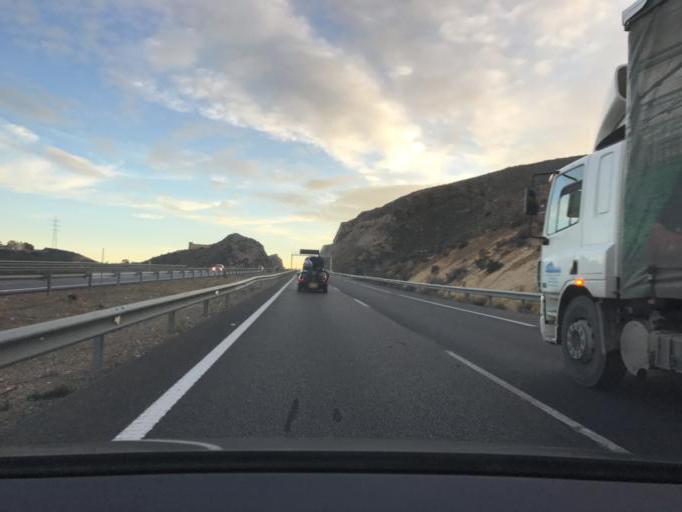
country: ES
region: Andalusia
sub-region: Provincia de Almeria
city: Huercal de Almeria
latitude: 36.8873
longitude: -2.4554
